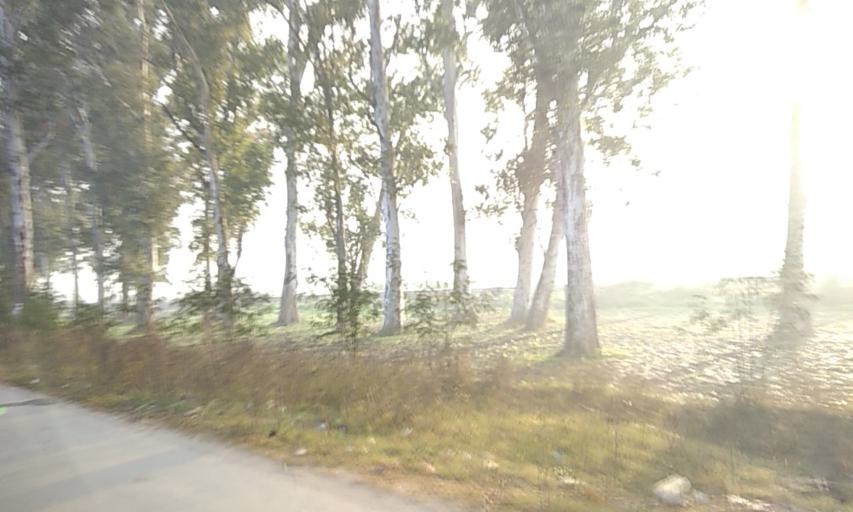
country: IN
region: Punjab
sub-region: Gurdaspur
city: Dhariwal
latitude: 31.9374
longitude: 75.3088
